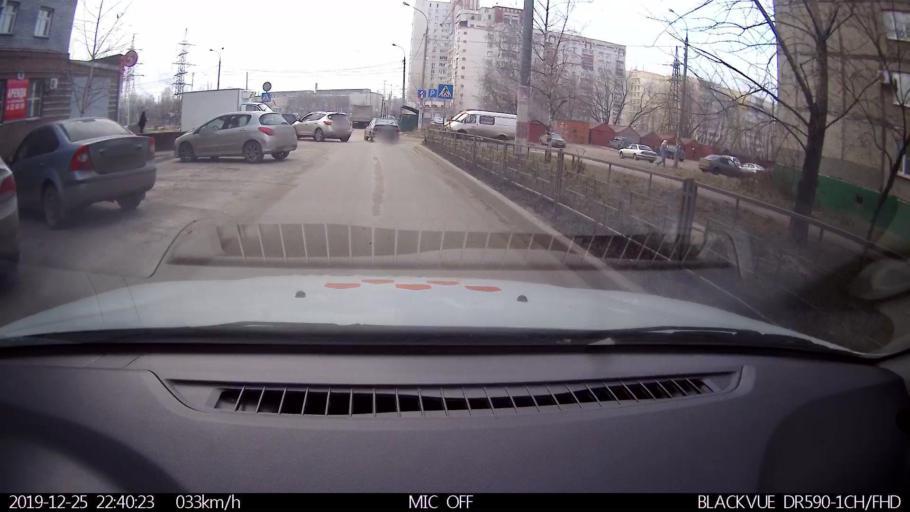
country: RU
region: Nizjnij Novgorod
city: Nizhniy Novgorod
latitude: 56.3311
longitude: 43.8718
